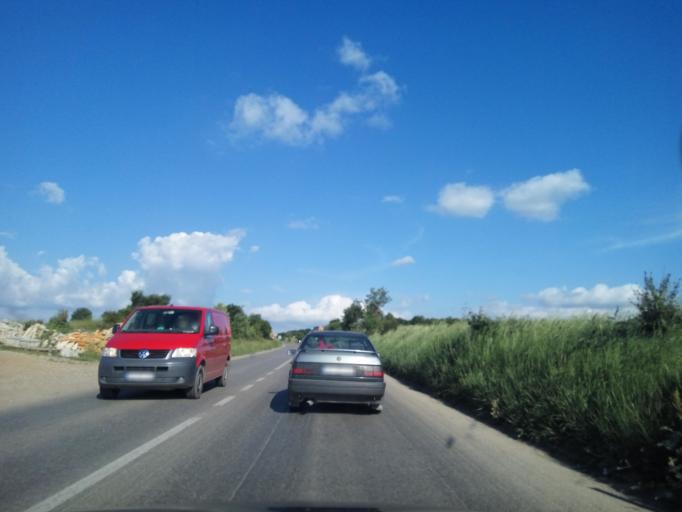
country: XK
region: Prizren
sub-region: Komuna e Malisheves
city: Llazice
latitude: 42.5881
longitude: 20.6713
